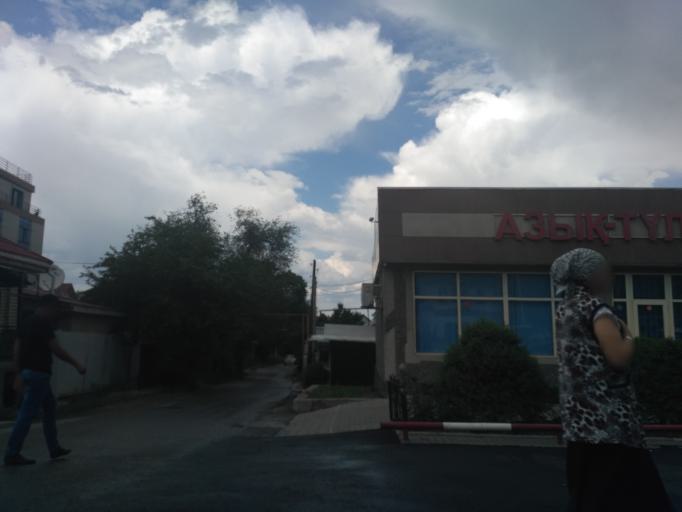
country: KZ
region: Almaty Oblysy
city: Burunday
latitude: 43.2028
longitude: 76.6211
